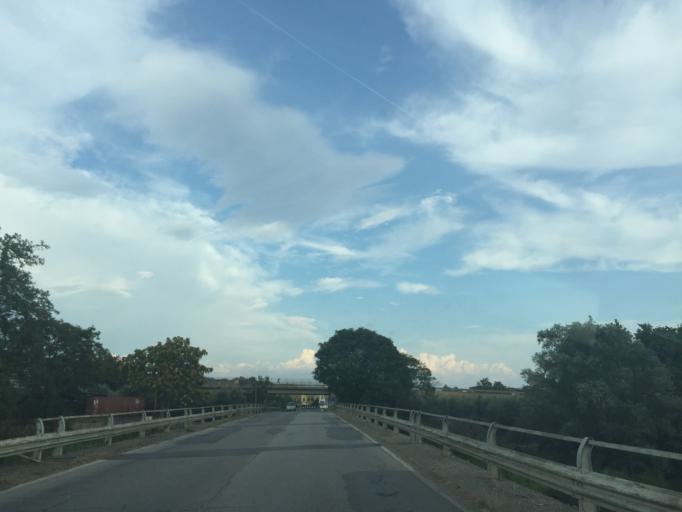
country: IT
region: Tuscany
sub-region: Provincia di Pistoia
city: Pistoia
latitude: 43.9571
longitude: 10.8968
